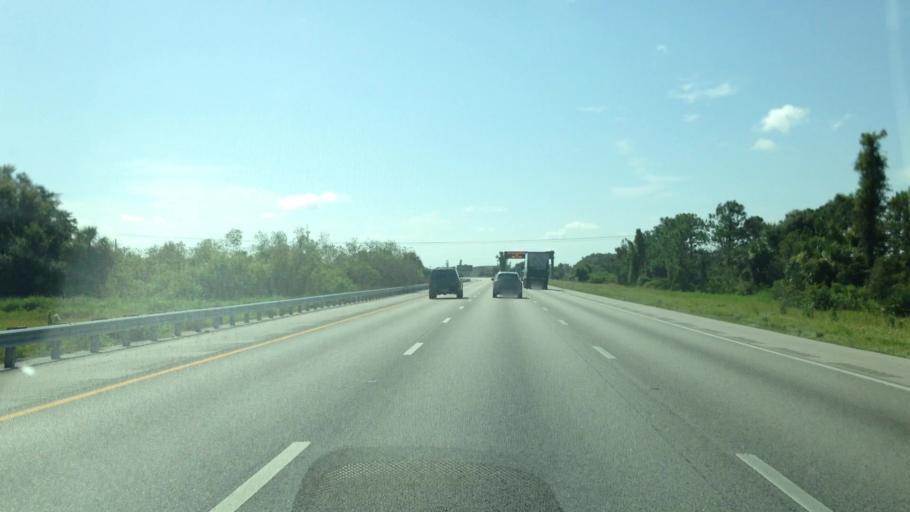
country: US
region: Florida
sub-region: Lee County
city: Suncoast Estates
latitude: 26.7282
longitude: -81.8380
